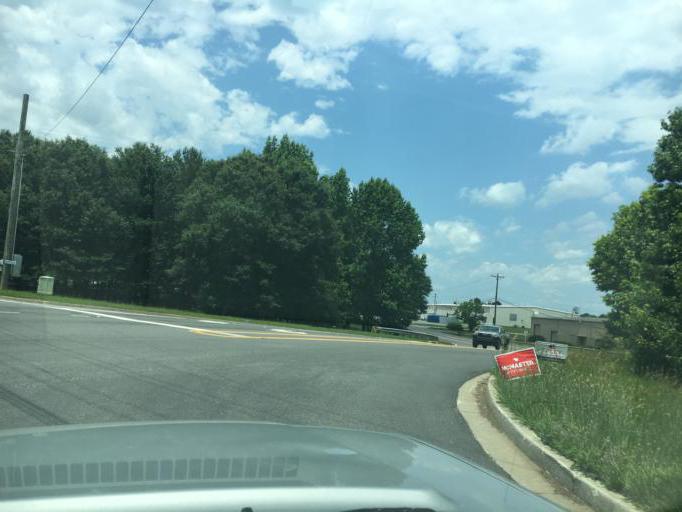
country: US
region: South Carolina
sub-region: Greenville County
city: Five Forks
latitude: 34.8529
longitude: -82.2322
